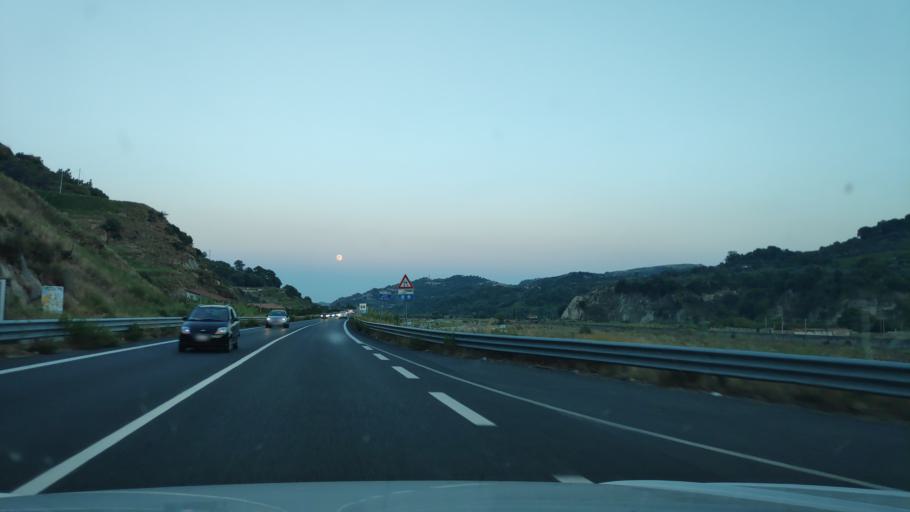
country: IT
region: Calabria
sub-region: Provincia di Reggio Calabria
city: Mammola
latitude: 38.3553
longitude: 16.2416
